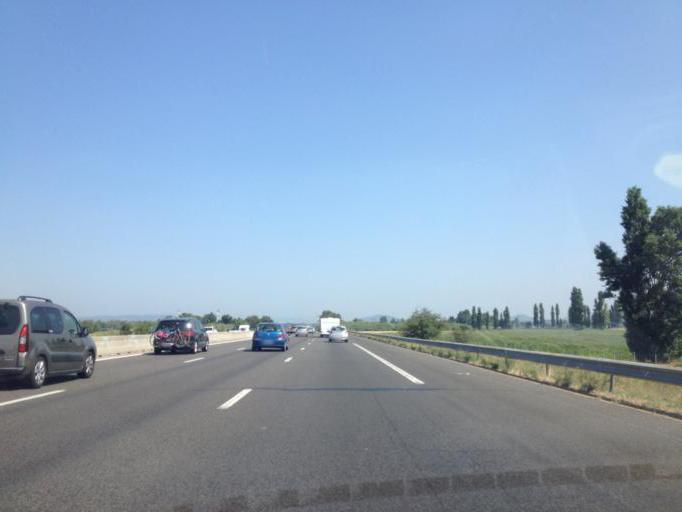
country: FR
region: Rhone-Alpes
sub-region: Departement de la Drome
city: Saint-Paul-Trois-Chateaux
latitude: 44.3601
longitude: 4.7369
